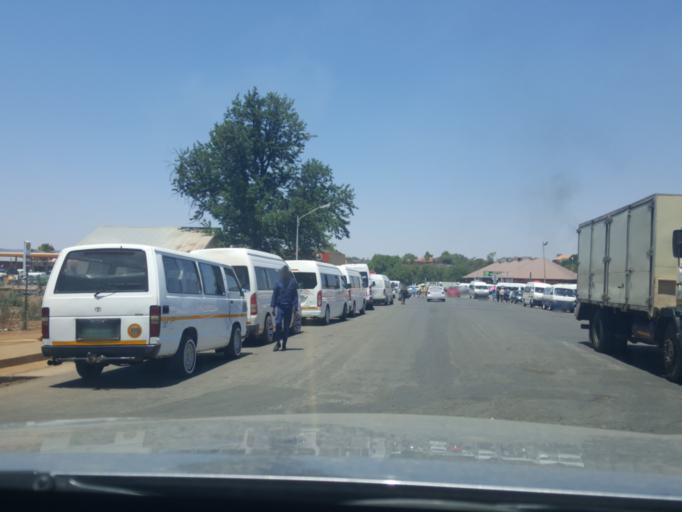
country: ZA
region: North-West
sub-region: Ngaka Modiri Molema District Municipality
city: Zeerust
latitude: -25.5452
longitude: 26.0745
